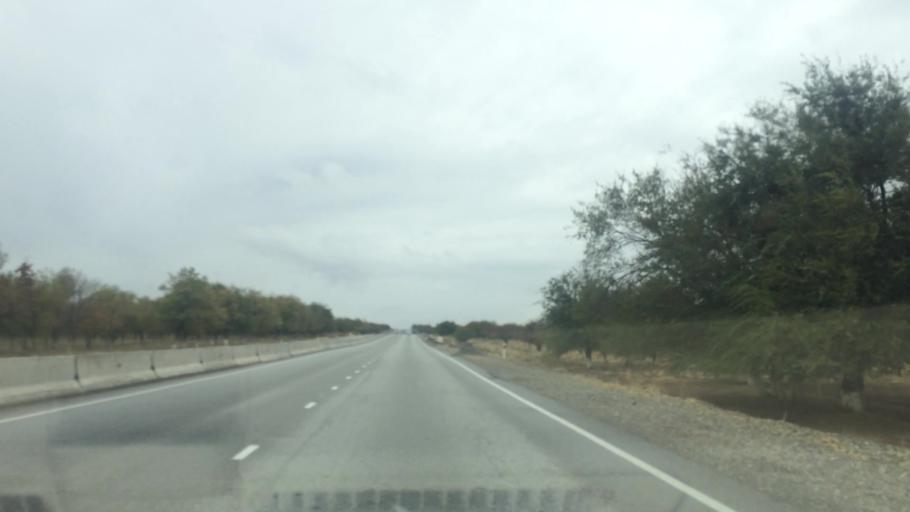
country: UZ
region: Samarqand
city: Bulung'ur
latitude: 39.8679
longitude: 67.4759
